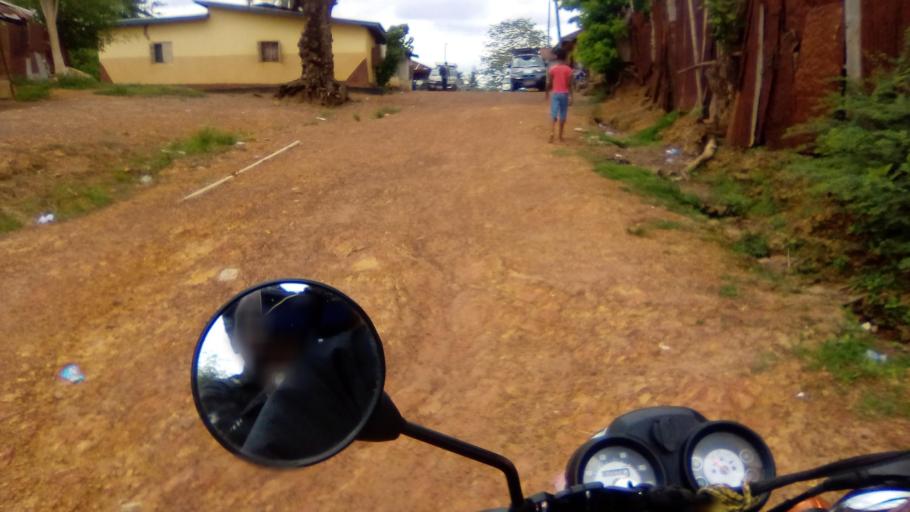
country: SL
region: Southern Province
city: Bo
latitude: 7.9627
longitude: -11.7311
